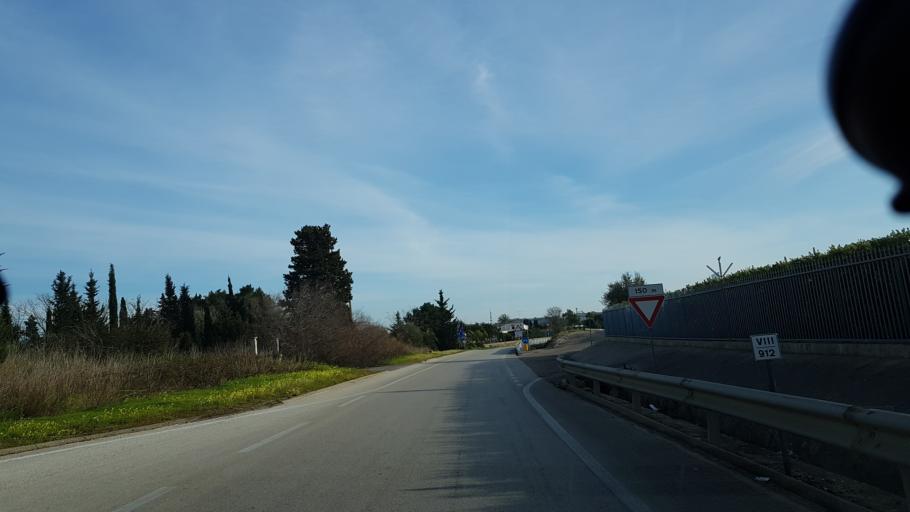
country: IT
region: Apulia
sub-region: Provincia di Brindisi
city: Brindisi
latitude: 40.6428
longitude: 17.9134
